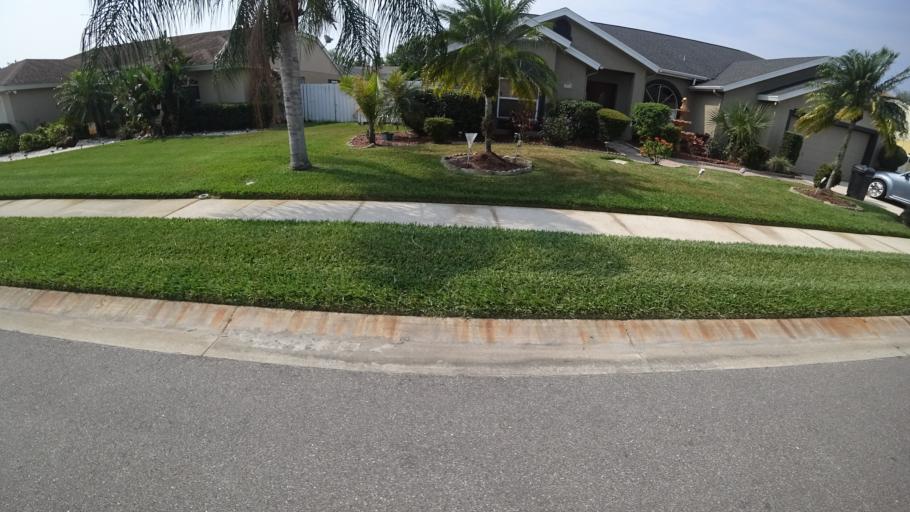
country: US
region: Florida
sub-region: Manatee County
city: Samoset
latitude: 27.4612
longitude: -82.5123
